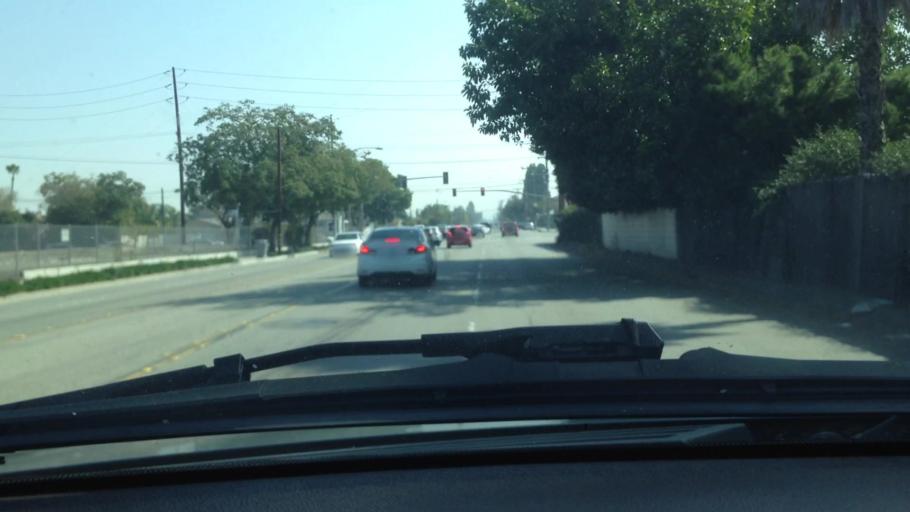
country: US
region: California
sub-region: Orange County
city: Anaheim
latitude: 33.8472
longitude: -117.9071
